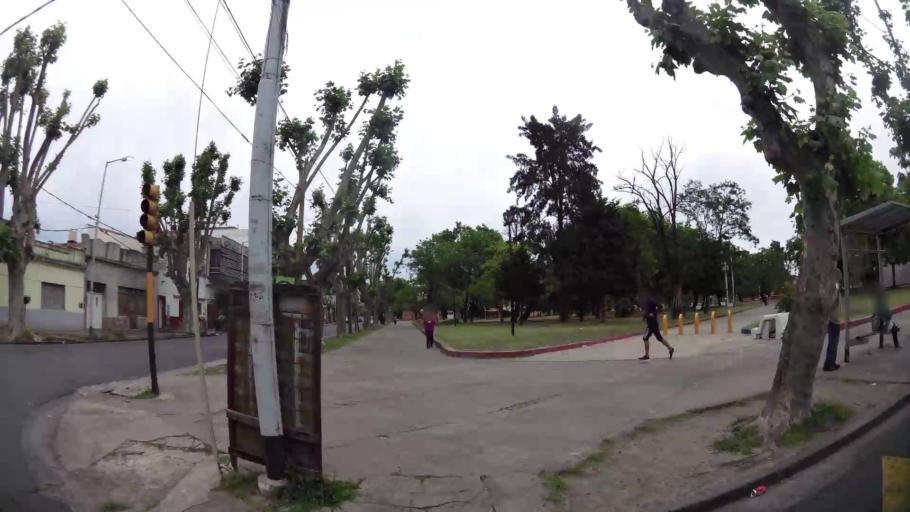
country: AR
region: Buenos Aires
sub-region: Partido de Avellaneda
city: Avellaneda
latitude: -34.6664
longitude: -58.3485
